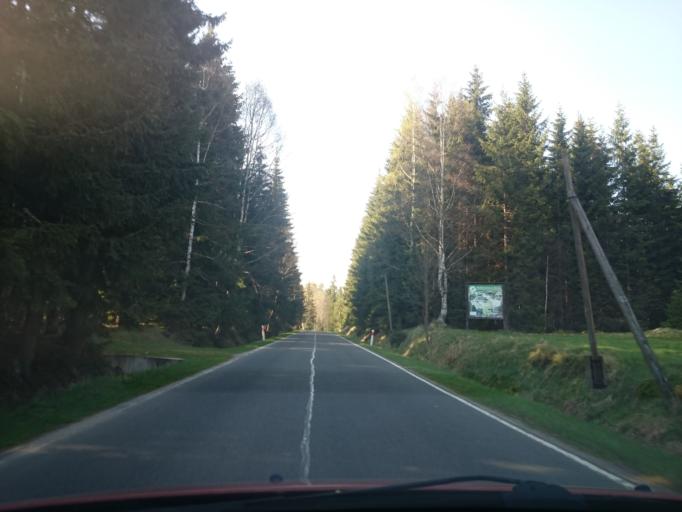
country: PL
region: Lower Silesian Voivodeship
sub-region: Powiat klodzki
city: Szczytna
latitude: 50.3190
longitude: 16.4406
